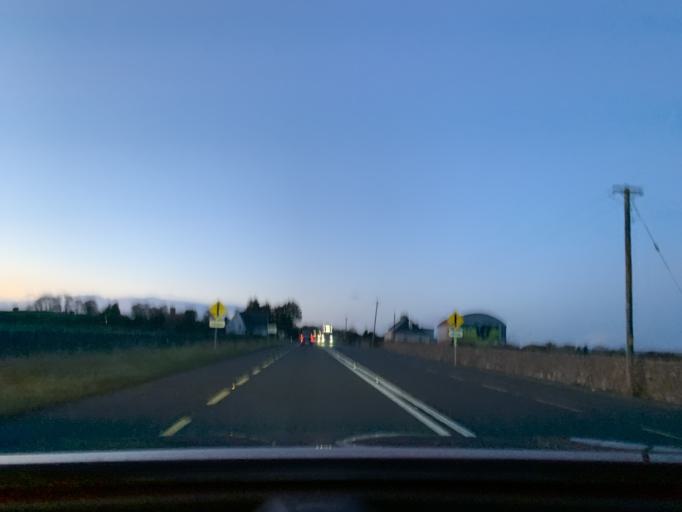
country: IE
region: Connaught
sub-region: Roscommon
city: Boyle
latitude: 53.9649
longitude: -8.1969
